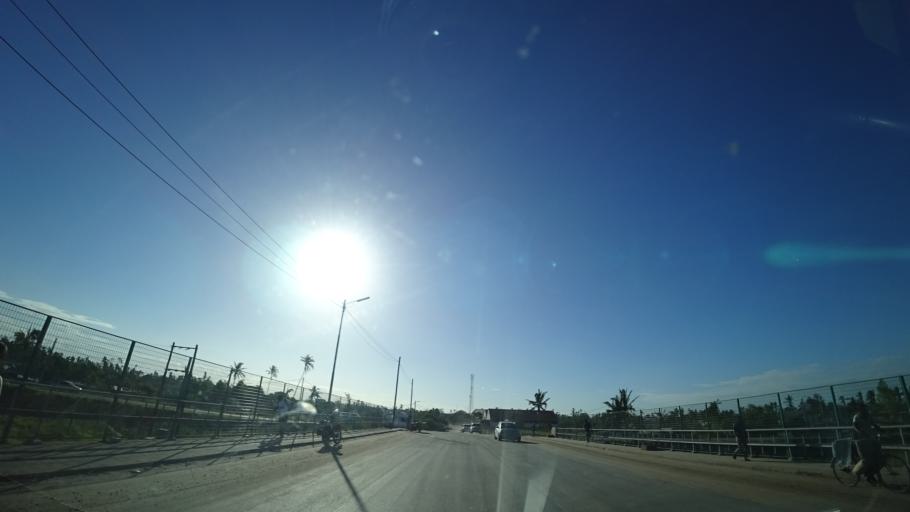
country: MZ
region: Sofala
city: Beira
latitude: -19.7829
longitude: 34.8785
